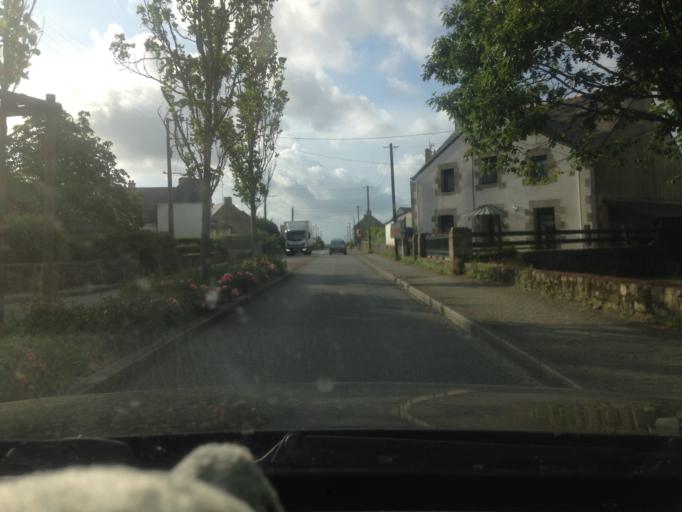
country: FR
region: Brittany
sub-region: Departement du Morbihan
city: Plouharnel
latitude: 47.5982
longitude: -3.1114
